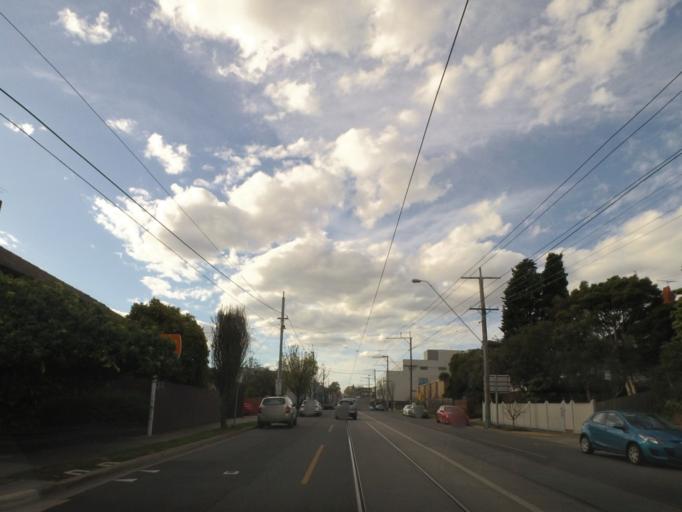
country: AU
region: Victoria
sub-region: Stonnington
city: Glen Iris
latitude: -37.8473
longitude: 145.0536
